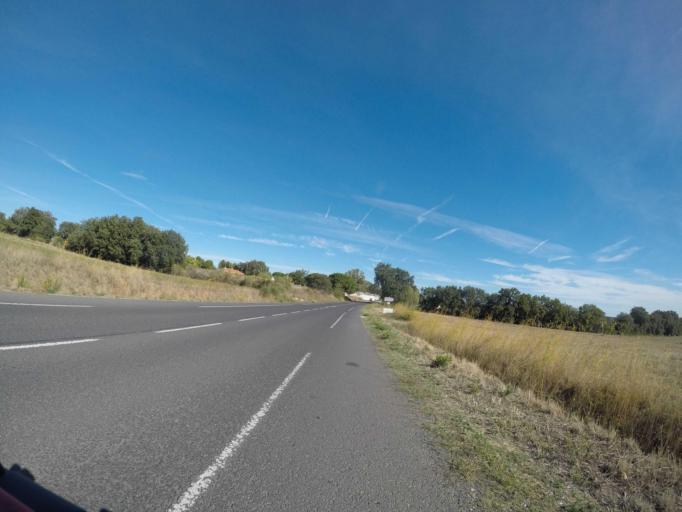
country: FR
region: Languedoc-Roussillon
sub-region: Departement des Pyrenees-Orientales
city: Ponteilla
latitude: 42.6219
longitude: 2.8116
